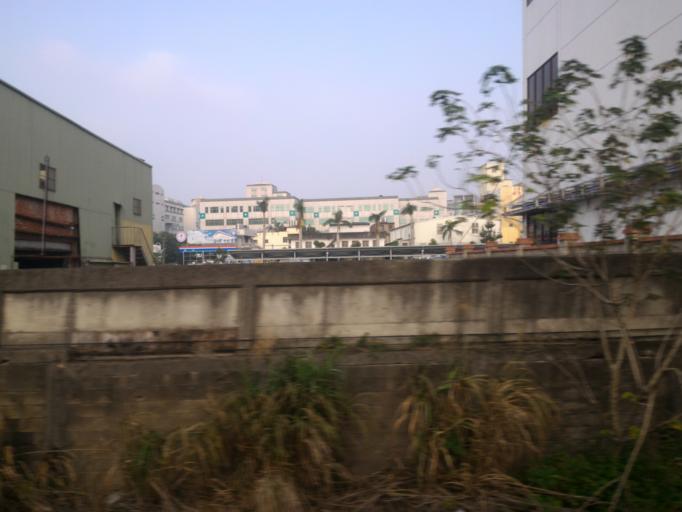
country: TW
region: Taiwan
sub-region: Taoyuan
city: Taoyuan
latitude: 24.9864
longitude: 121.3243
